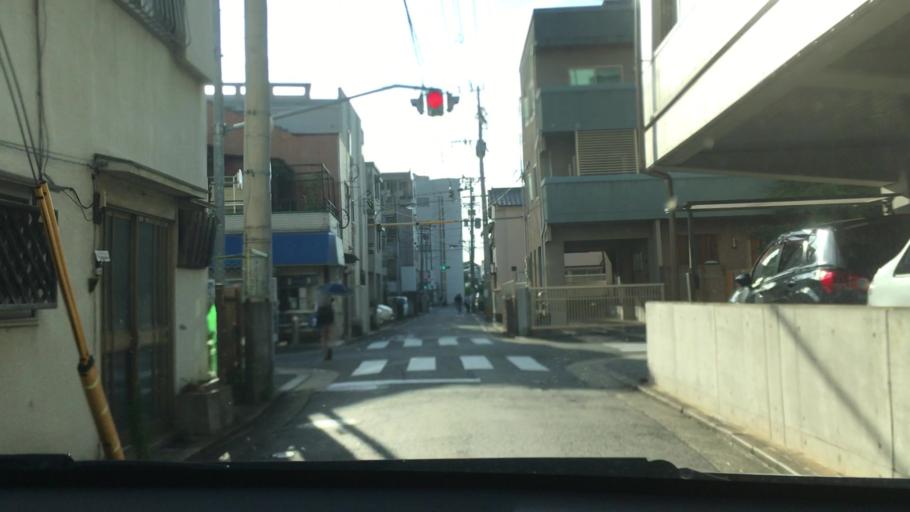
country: JP
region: Fukuoka
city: Fukuoka-shi
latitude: 33.6197
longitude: 130.4197
